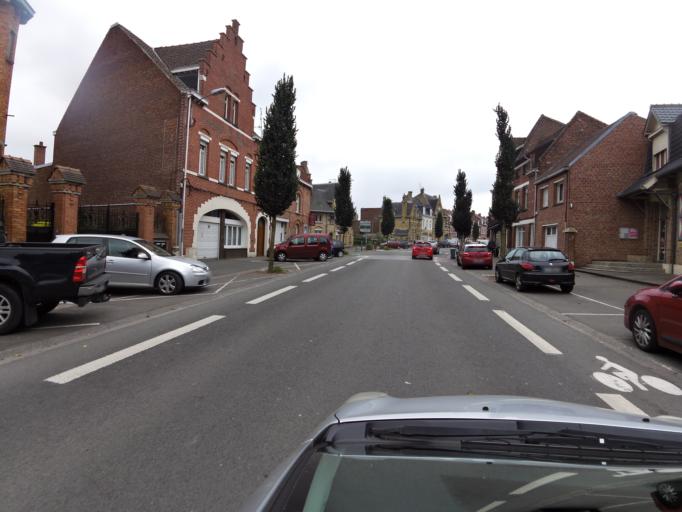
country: FR
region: Nord-Pas-de-Calais
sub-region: Departement du Nord
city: Bailleul
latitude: 50.7404
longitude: 2.7375
